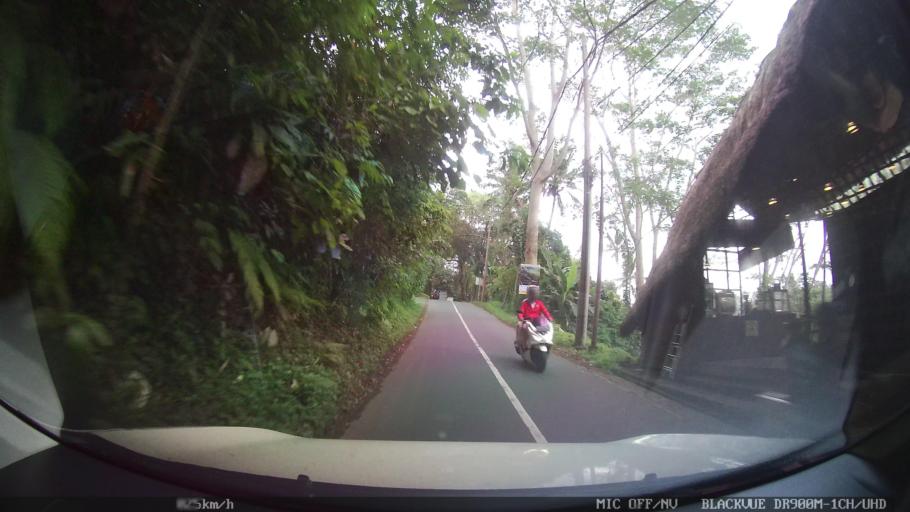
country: ID
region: Bali
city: Bunutan
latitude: -8.4806
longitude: 115.2559
